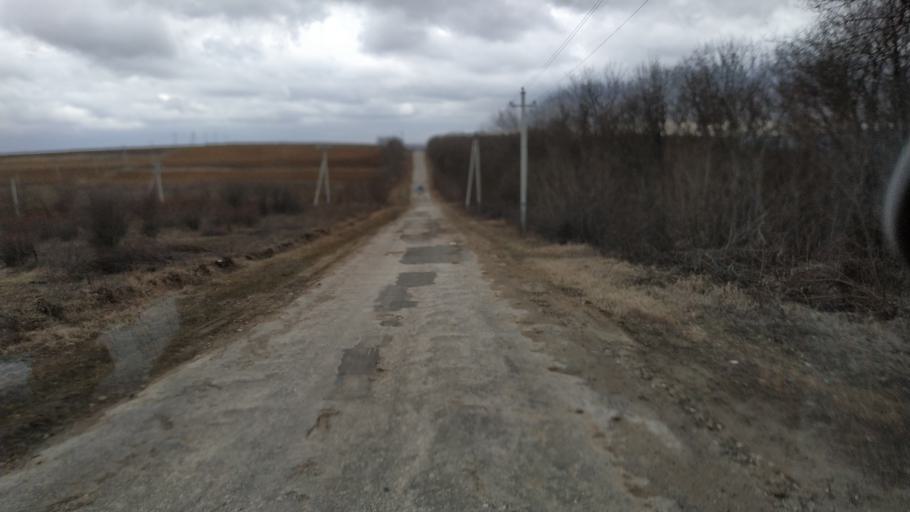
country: MD
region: Calarasi
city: Calarasi
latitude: 47.2267
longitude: 28.2492
